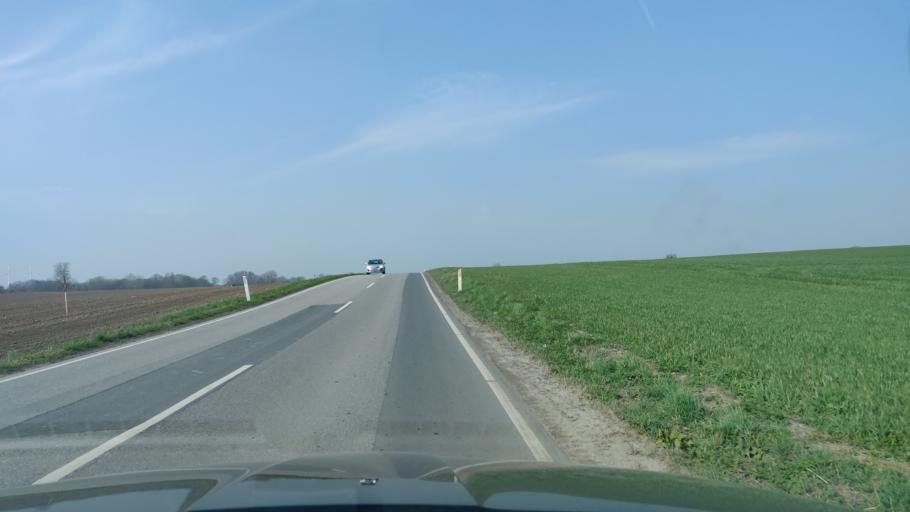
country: DK
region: South Denmark
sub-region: Nordfyns Kommune
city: Sonderso
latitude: 55.5158
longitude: 10.2658
